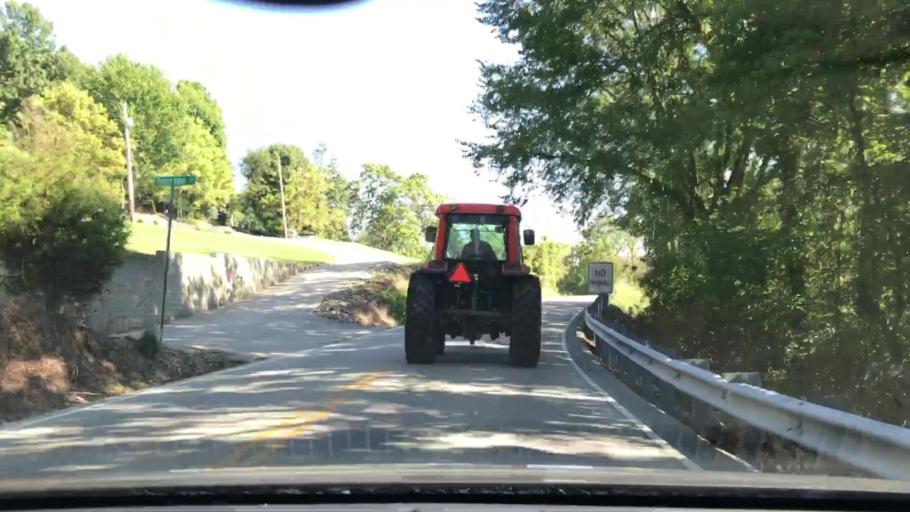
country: US
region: Tennessee
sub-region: Smith County
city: Carthage
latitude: 36.2982
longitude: -85.9538
